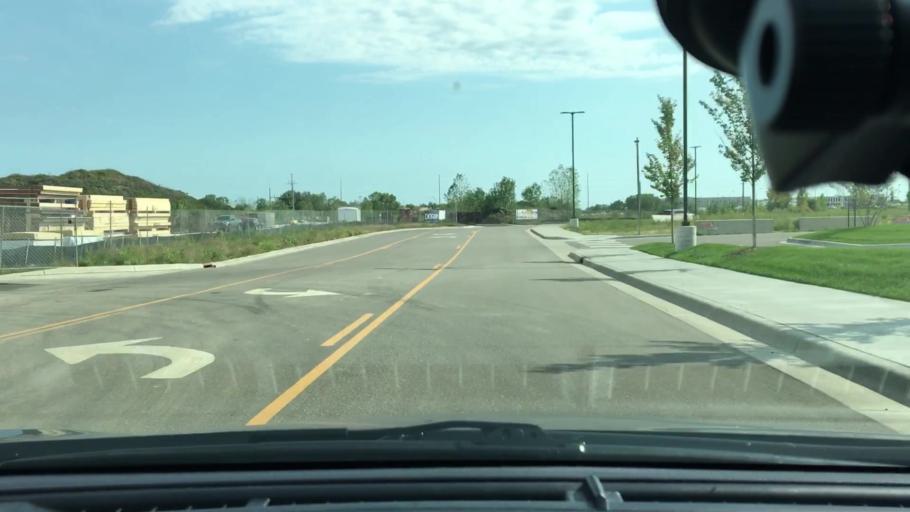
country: US
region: Minnesota
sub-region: Hennepin County
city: Osseo
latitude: 45.0959
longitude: -93.4284
